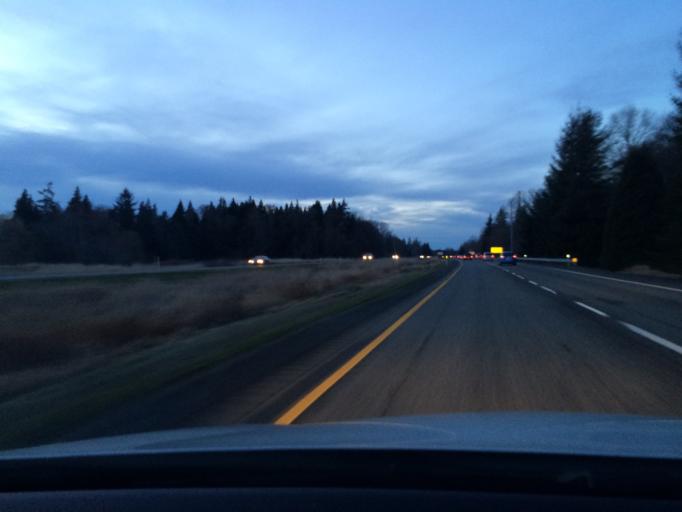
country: US
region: Washington
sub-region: Whatcom County
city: Blaine
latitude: 48.9606
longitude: -122.7005
